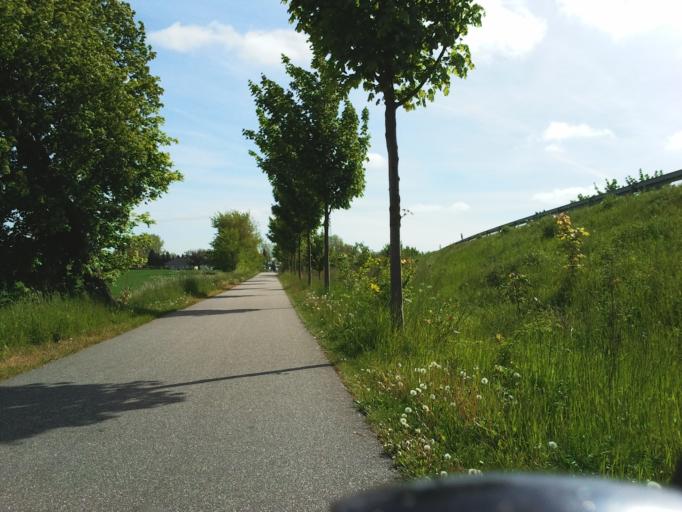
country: DE
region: Mecklenburg-Vorpommern
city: Papendorf
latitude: 54.0489
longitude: 12.1175
